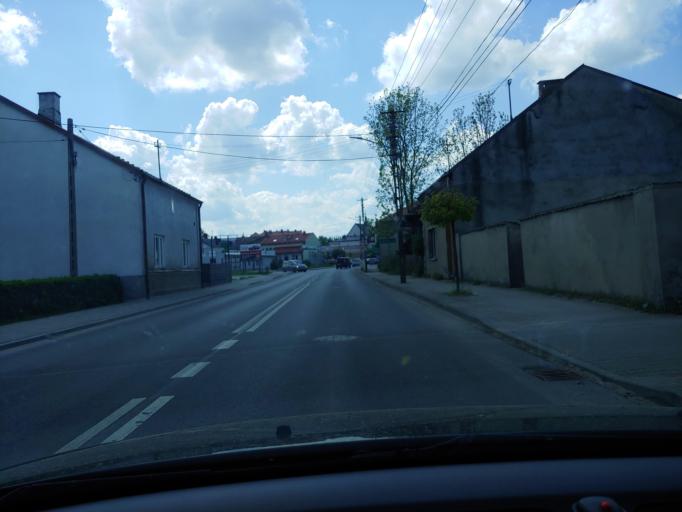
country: PL
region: Subcarpathian Voivodeship
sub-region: Powiat mielecki
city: Radomysl Wielki
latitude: 50.1981
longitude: 21.2783
